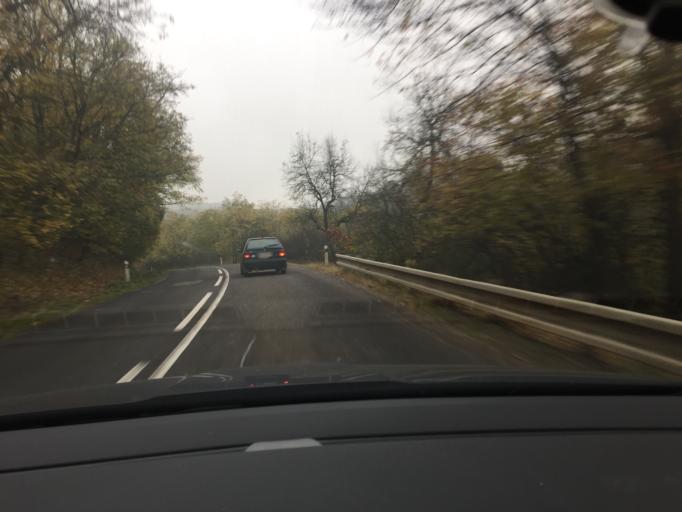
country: SK
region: Banskobystricky
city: Dudince
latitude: 48.1586
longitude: 18.9224
